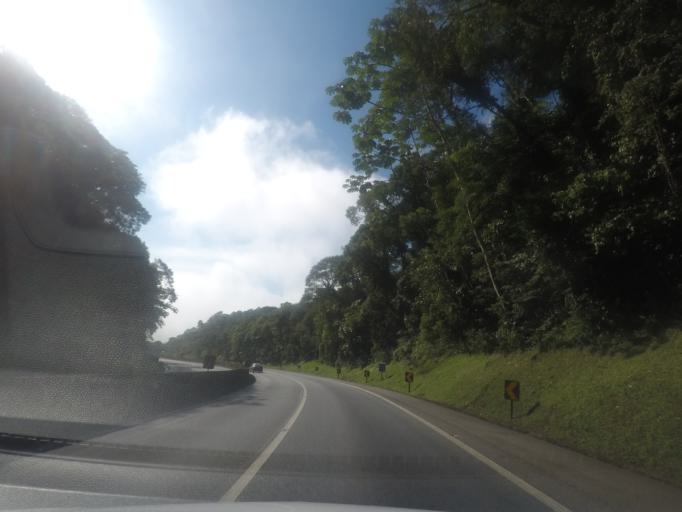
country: BR
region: Parana
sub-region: Piraquara
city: Piraquara
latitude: -25.5931
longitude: -48.8905
